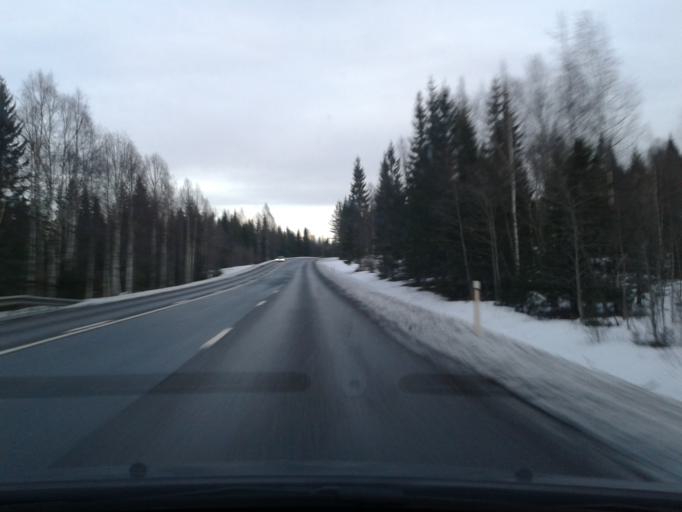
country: SE
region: Vaesternorrland
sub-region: Solleftea Kommun
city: Solleftea
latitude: 63.1375
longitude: 17.4436
